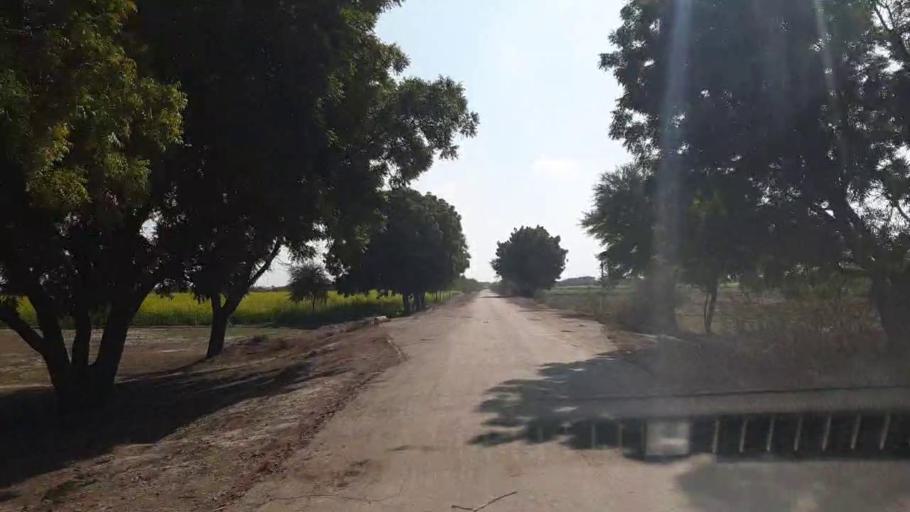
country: PK
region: Sindh
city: Shahpur Chakar
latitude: 26.0504
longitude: 68.6057
